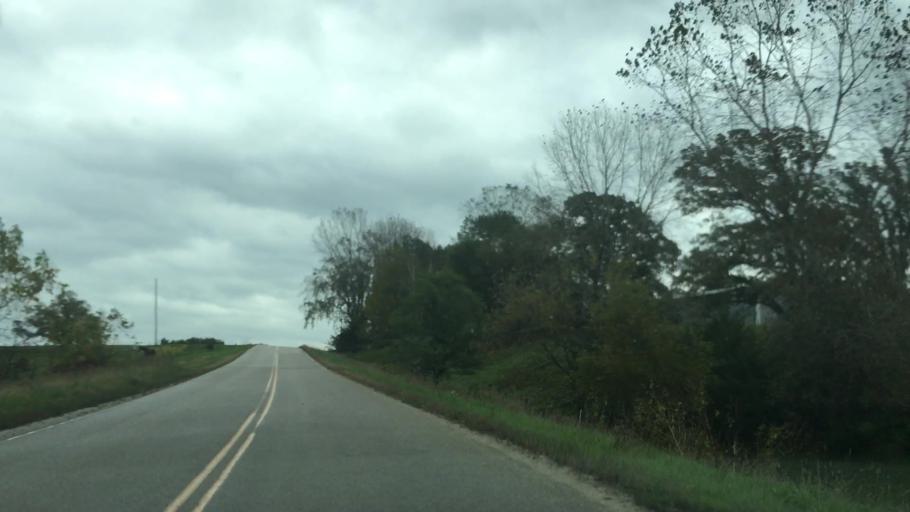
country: US
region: Minnesota
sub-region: Fillmore County
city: Preston
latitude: 43.7421
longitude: -92.0153
